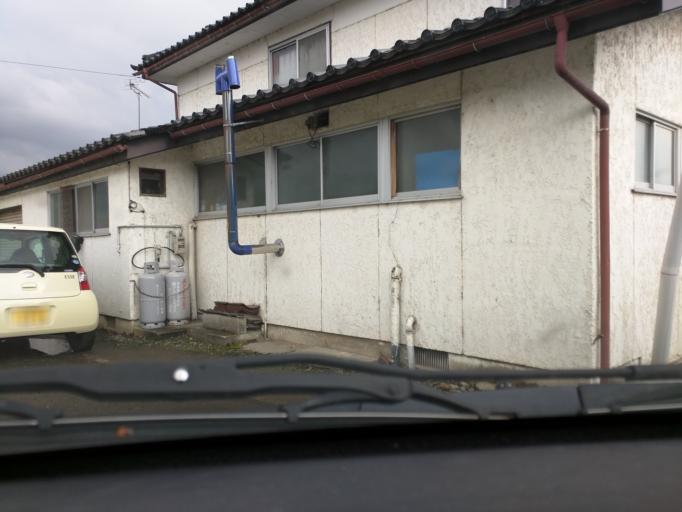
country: JP
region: Fukushima
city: Kitakata
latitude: 37.6435
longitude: 139.9298
